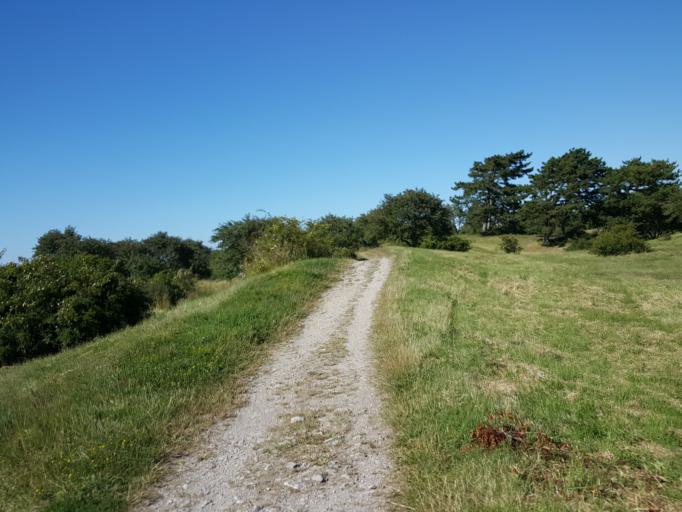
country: SE
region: Gotland
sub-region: Gotland
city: Visby
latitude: 57.6431
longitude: 18.3022
